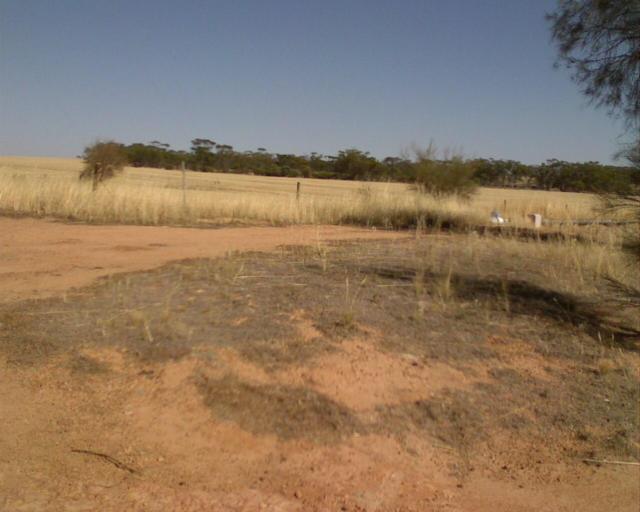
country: AU
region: Western Australia
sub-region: Merredin
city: Merredin
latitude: -31.4249
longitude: 117.7508
